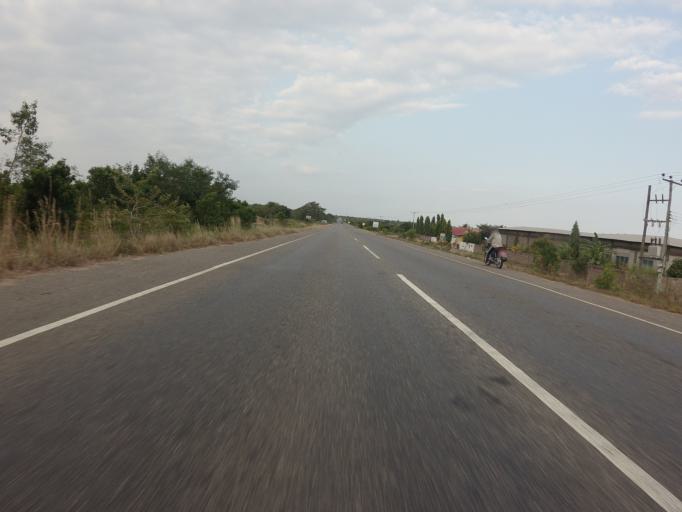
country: GH
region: Volta
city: Anloga
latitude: 6.0879
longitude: 0.5121
